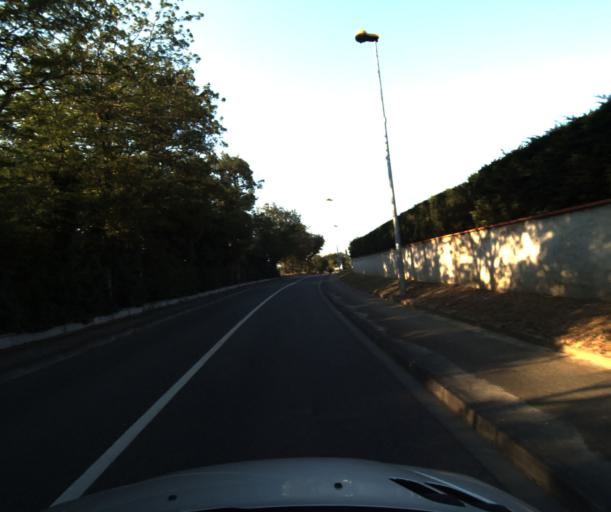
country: FR
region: Midi-Pyrenees
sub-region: Departement de la Haute-Garonne
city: Roquettes
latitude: 43.4849
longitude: 1.3894
